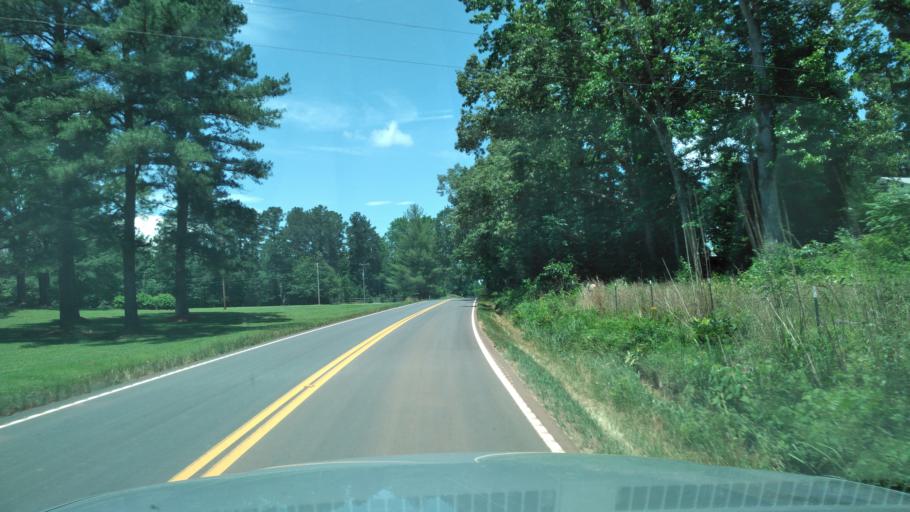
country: US
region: South Carolina
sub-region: Greenwood County
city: Ware Shoals
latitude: 34.4135
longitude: -82.1319
